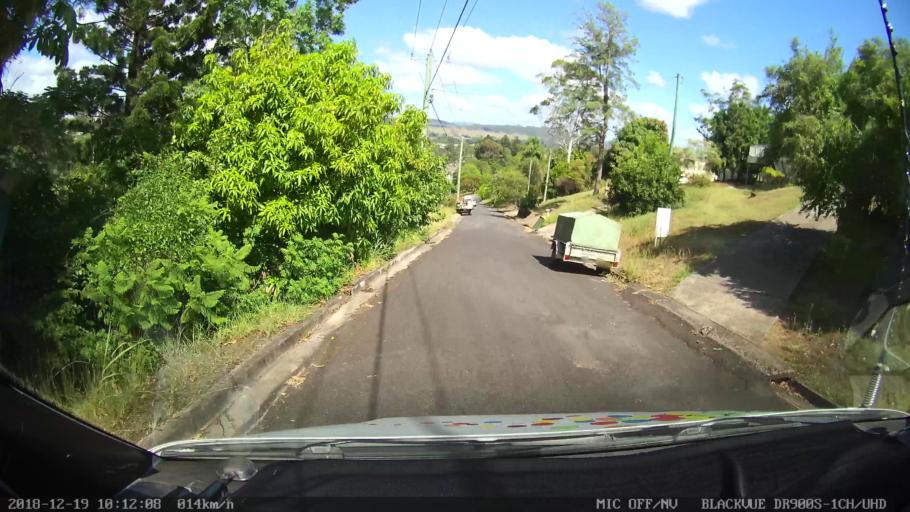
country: AU
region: New South Wales
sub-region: Kyogle
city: Kyogle
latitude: -28.6200
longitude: 153.0085
